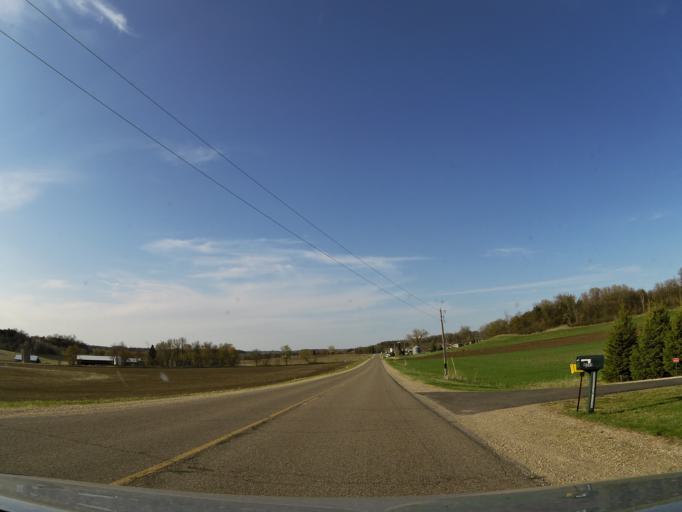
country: US
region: Wisconsin
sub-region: Pierce County
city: River Falls
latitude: 44.7923
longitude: -92.6469
